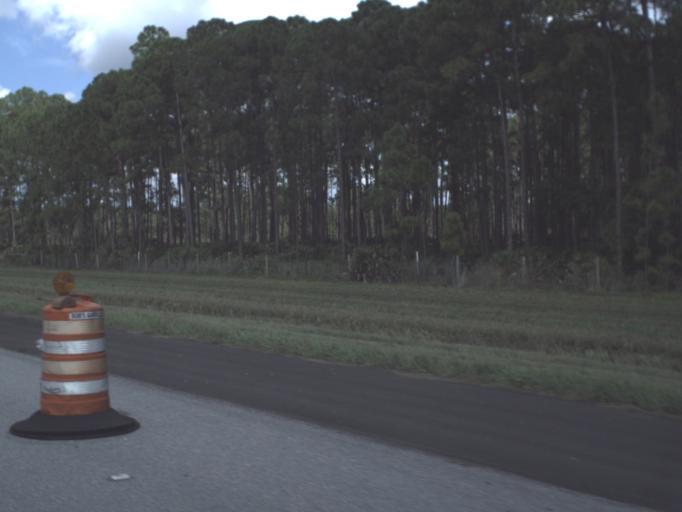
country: US
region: Florida
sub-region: Sarasota County
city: Warm Mineral Springs
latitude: 27.1001
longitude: -82.2604
